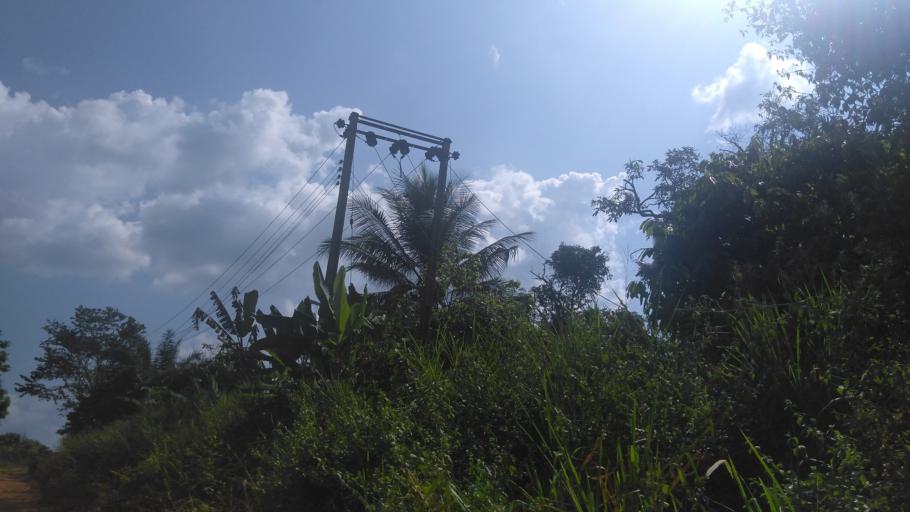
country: NG
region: Osun
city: Ifetedo
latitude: 7.0240
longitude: 4.6302
